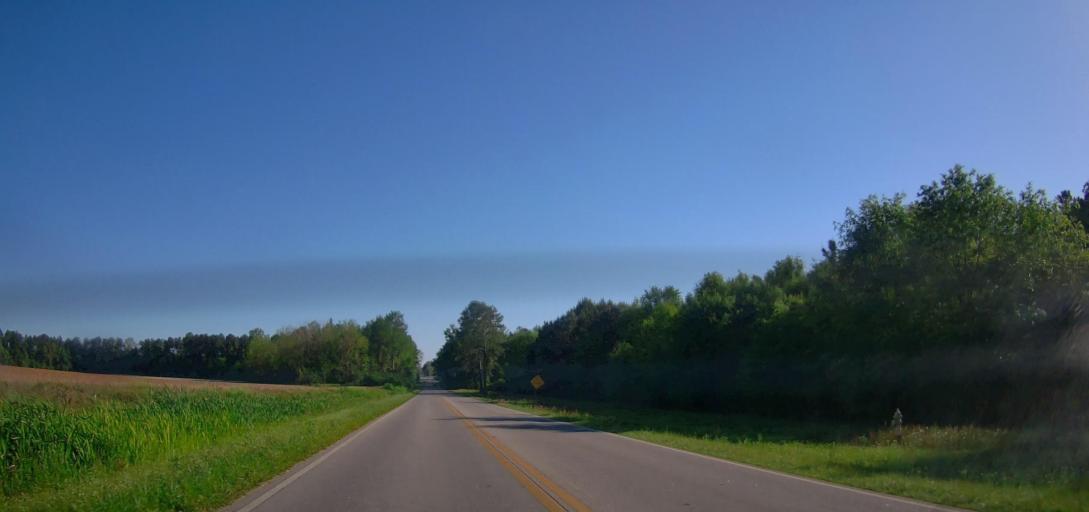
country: US
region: Georgia
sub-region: Ben Hill County
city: Fitzgerald
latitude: 31.7212
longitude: -83.2355
